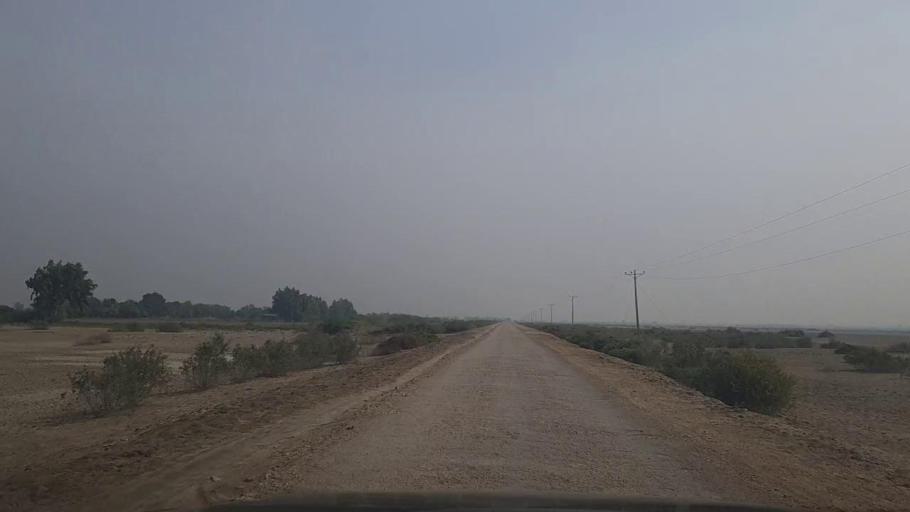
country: PK
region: Sindh
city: Mirpur Sakro
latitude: 24.4611
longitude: 67.6934
